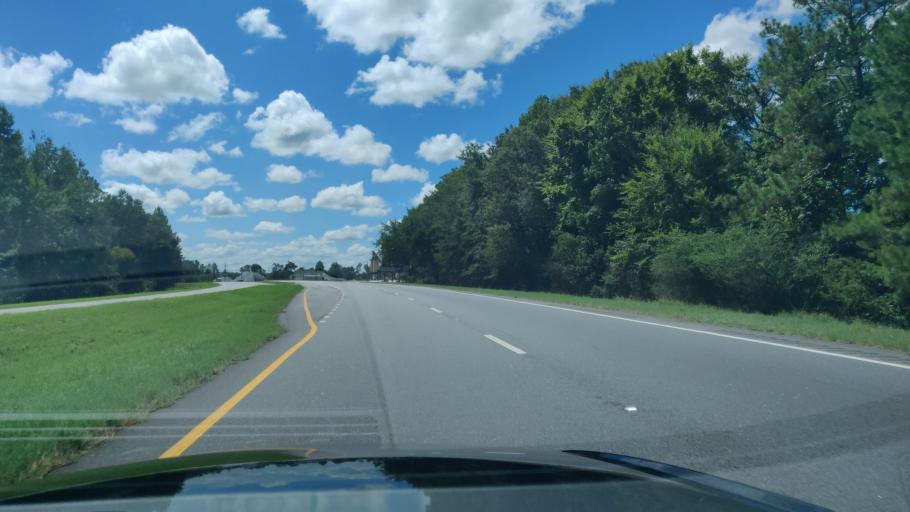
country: US
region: Georgia
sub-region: Terrell County
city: Dawson
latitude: 31.7350
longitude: -84.3719
